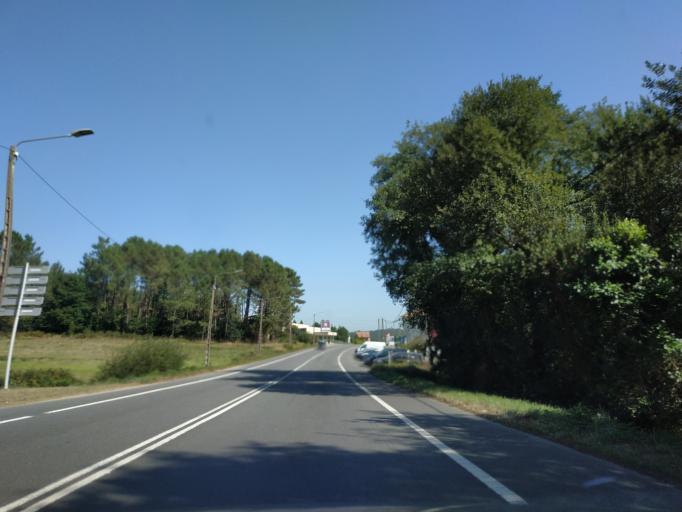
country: ES
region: Galicia
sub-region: Provincia da Coruna
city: Carballo
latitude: 43.2304
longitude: -8.6618
